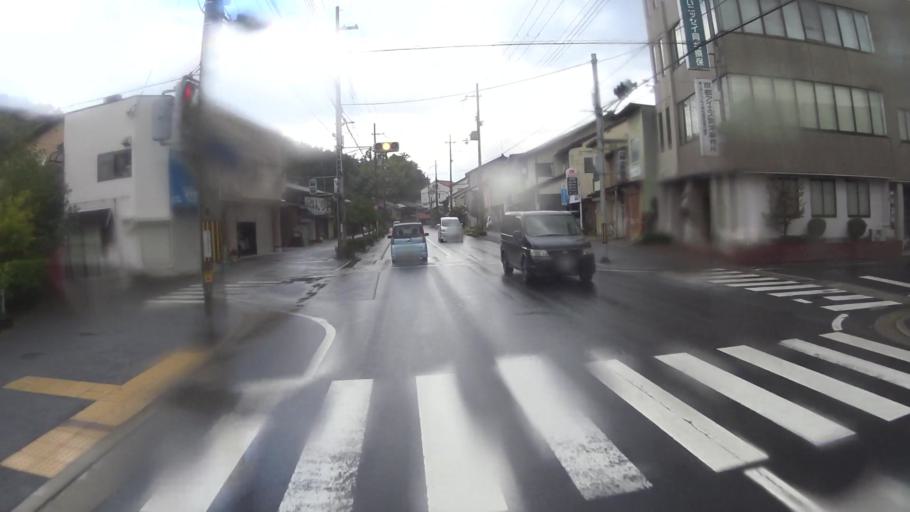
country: JP
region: Kyoto
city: Miyazu
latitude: 35.5413
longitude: 135.1897
